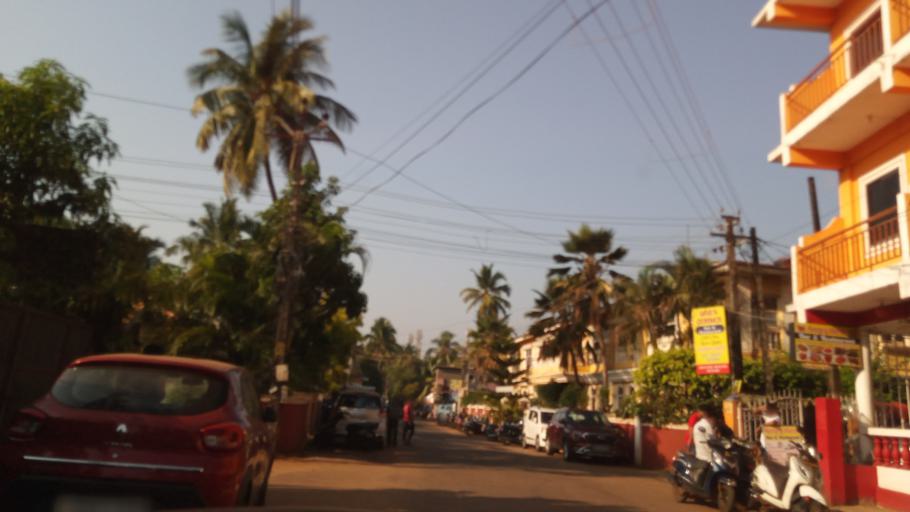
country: IN
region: Goa
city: Calangute
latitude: 15.5403
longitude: 73.7609
